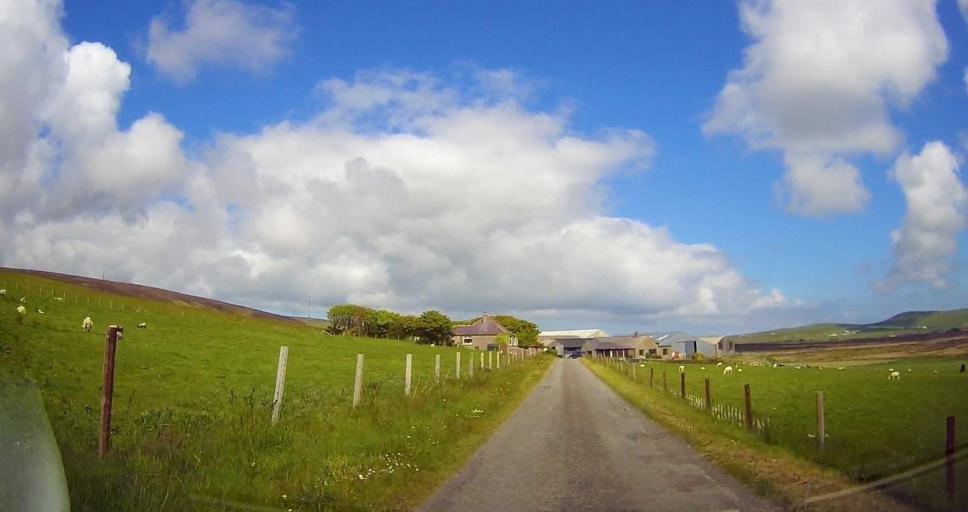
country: GB
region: Scotland
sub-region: Orkney Islands
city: Orkney
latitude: 59.0560
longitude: -3.1019
